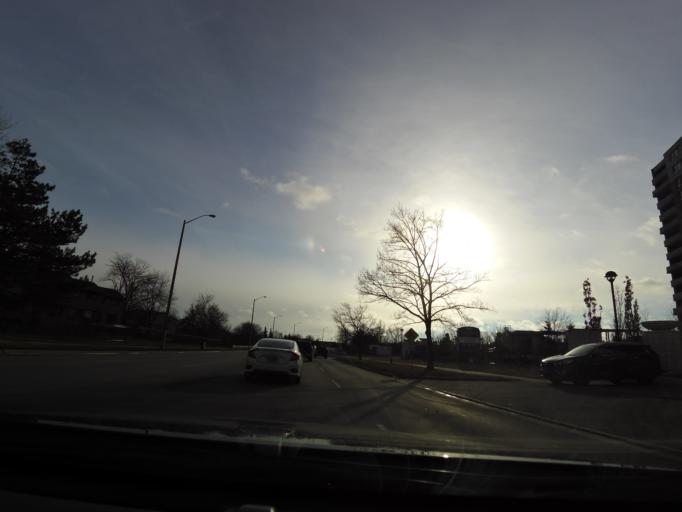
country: CA
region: Ontario
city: Brampton
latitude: 43.7087
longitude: -79.7246
